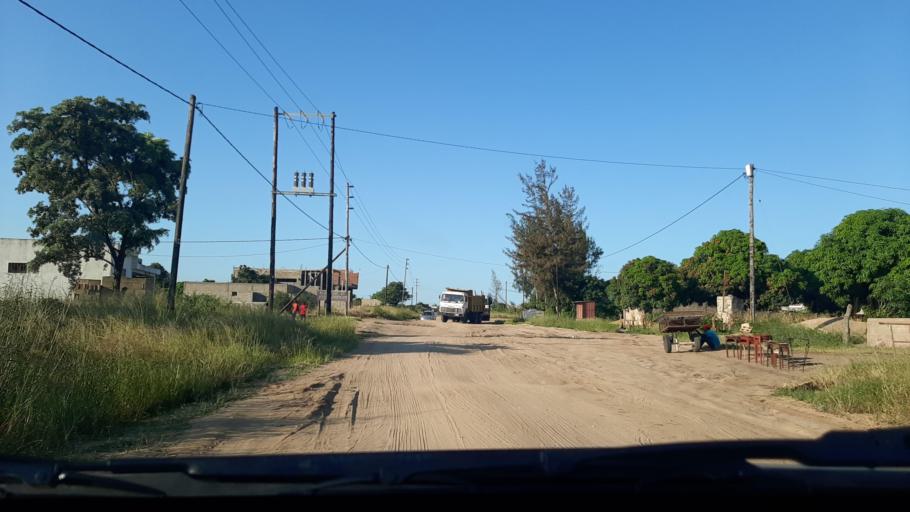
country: MZ
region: Maputo City
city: Maputo
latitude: -25.7608
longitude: 32.5488
